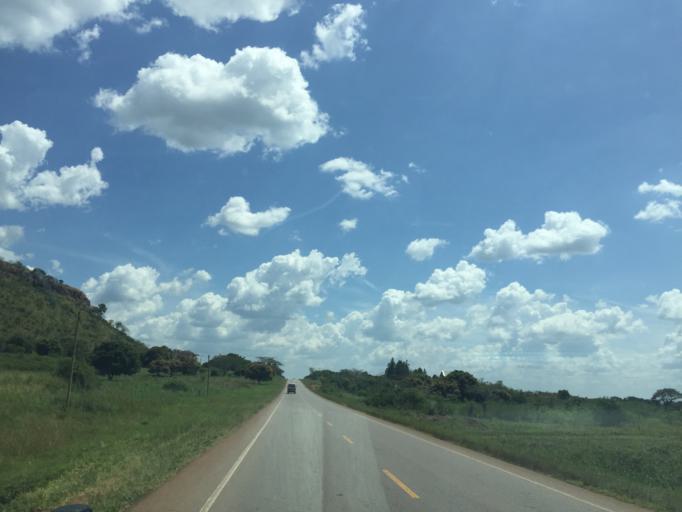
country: UG
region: Central Region
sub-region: Nakasongola District
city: Nakasongola
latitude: 1.3152
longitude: 32.4221
